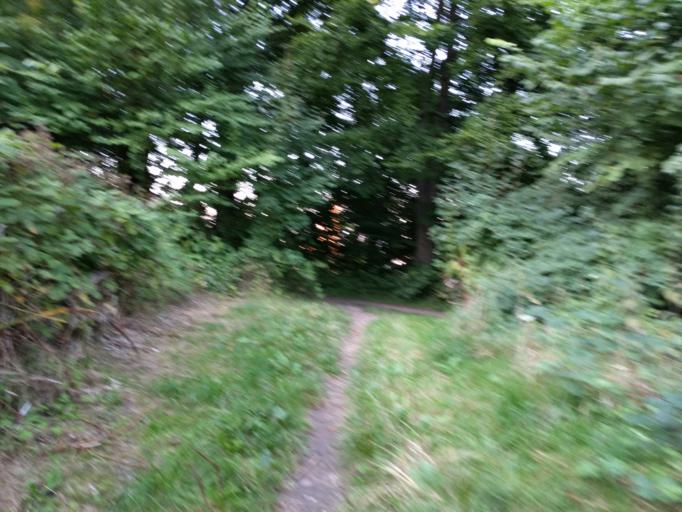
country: DK
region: South Denmark
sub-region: Odense Kommune
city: Odense
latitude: 55.4139
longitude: 10.3757
